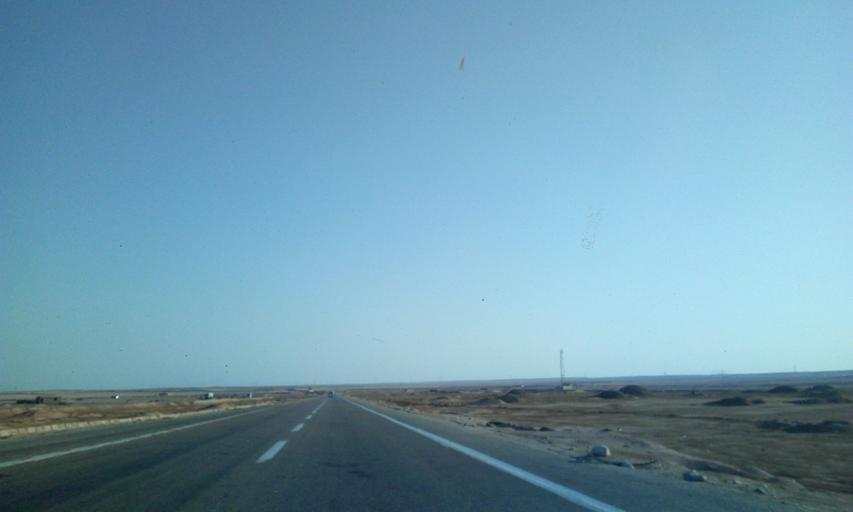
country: EG
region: South Sinai
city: Tor
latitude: 28.5839
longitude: 32.8627
